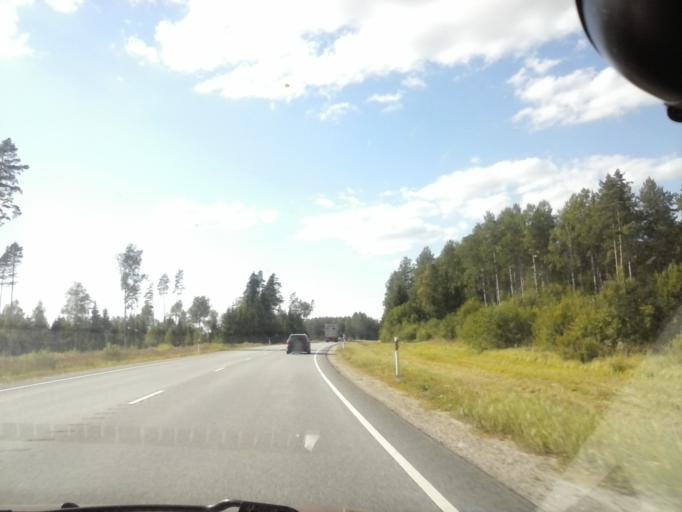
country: EE
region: Jogevamaa
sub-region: Poltsamaa linn
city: Poltsamaa
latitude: 58.6225
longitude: 26.1601
